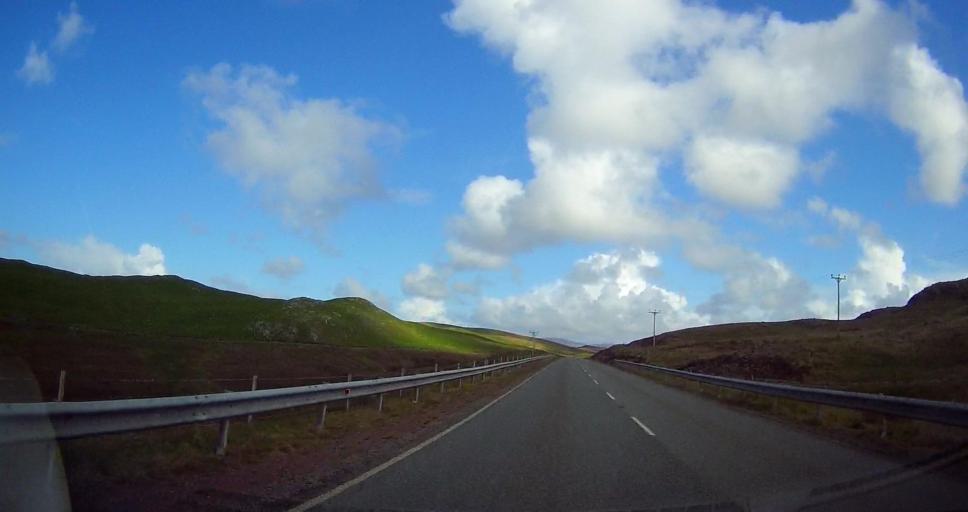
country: GB
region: Scotland
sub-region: Shetland Islands
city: Lerwick
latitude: 60.4212
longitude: -1.3942
